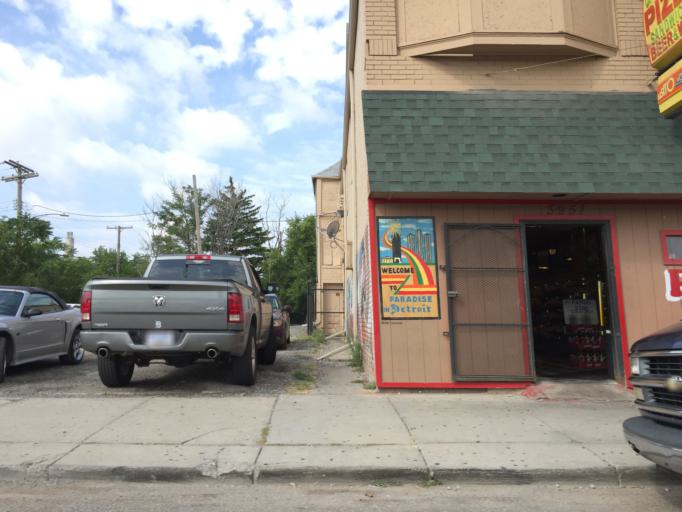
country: US
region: Michigan
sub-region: Wayne County
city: Hamtramck
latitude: 42.3737
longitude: -83.0462
